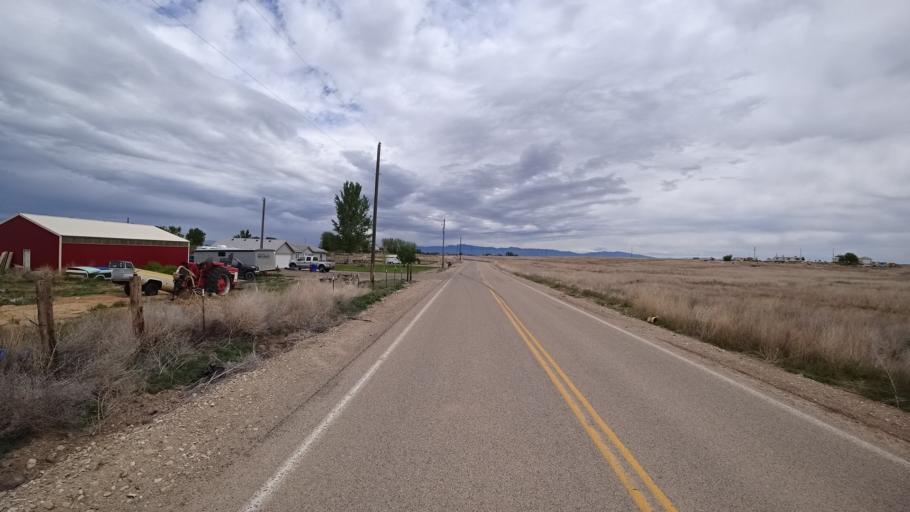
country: US
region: Idaho
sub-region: Ada County
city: Kuna
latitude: 43.4705
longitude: -116.4374
